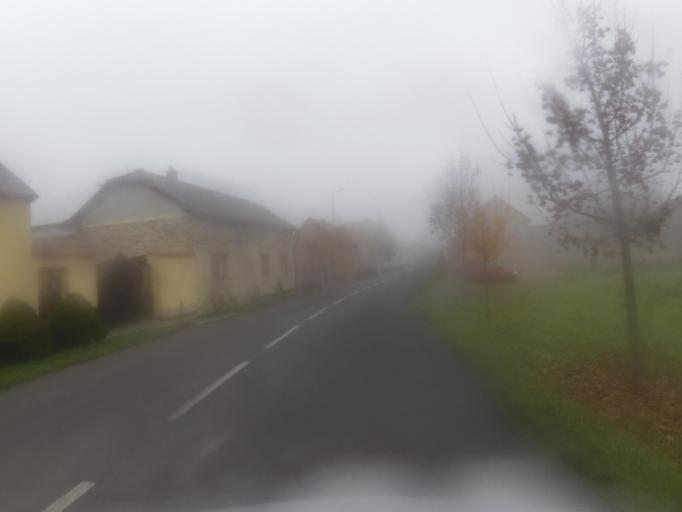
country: CZ
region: Ustecky
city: Cerncice
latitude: 50.3718
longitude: 13.8595
